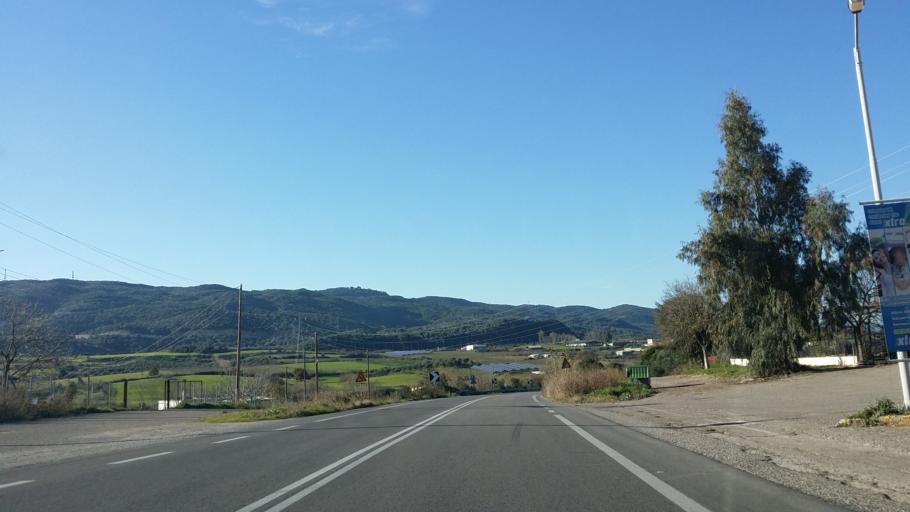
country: GR
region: West Greece
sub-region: Nomos Aitolias kai Akarnanias
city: Fitiai
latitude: 38.6893
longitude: 21.2289
